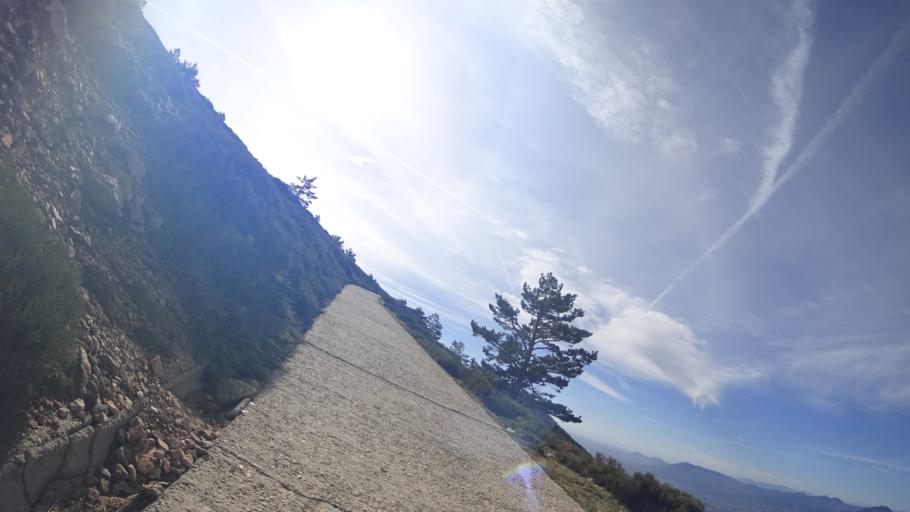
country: ES
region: Madrid
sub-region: Provincia de Madrid
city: Navacerrada
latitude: 40.7863
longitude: -3.9969
